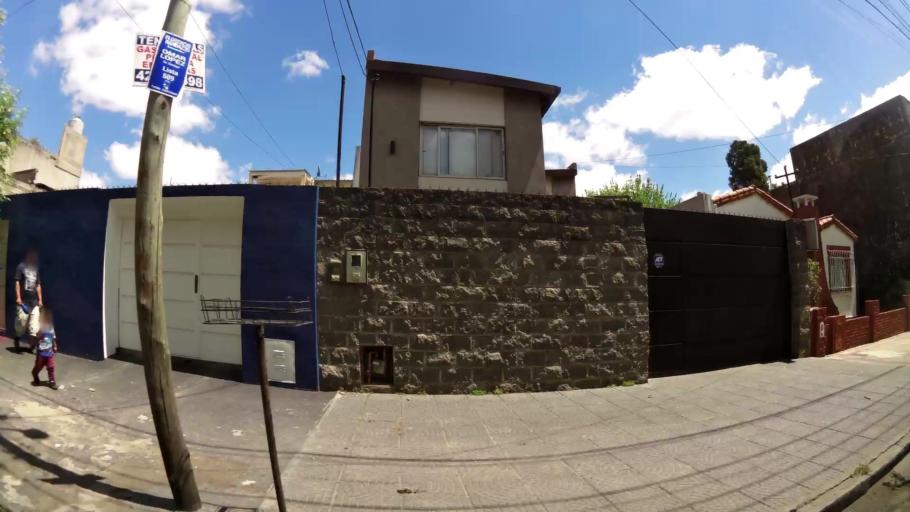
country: AR
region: Buenos Aires
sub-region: Partido de Lanus
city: Lanus
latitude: -34.7270
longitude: -58.4062
